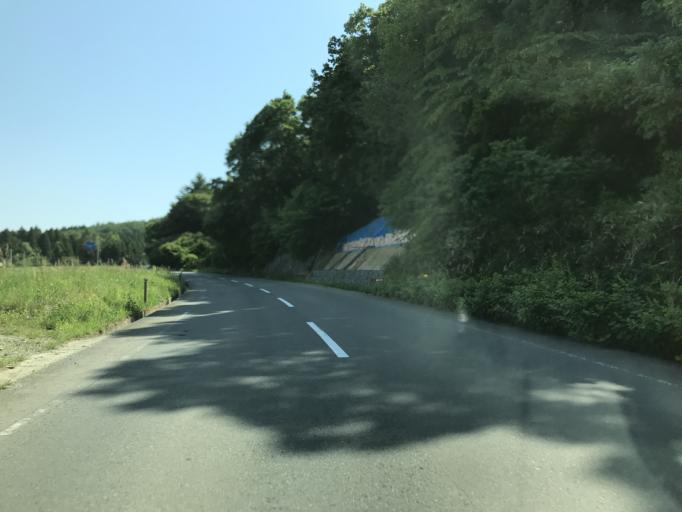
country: JP
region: Miyagi
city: Marumori
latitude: 37.8008
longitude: 140.8816
